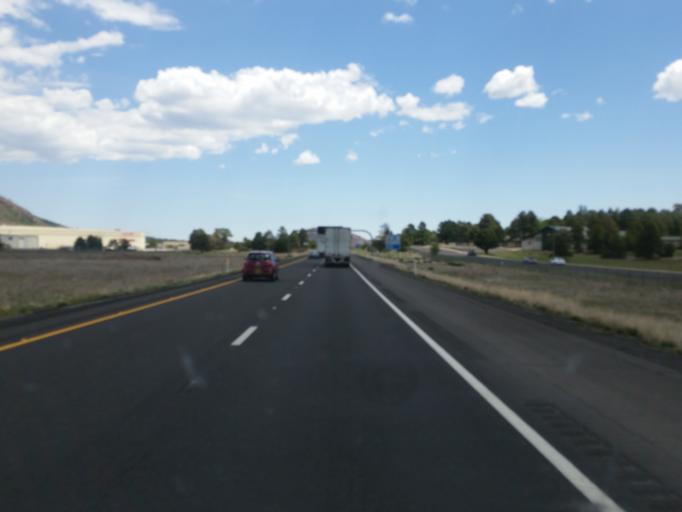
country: US
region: Arizona
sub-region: Coconino County
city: Flagstaff
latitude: 35.2049
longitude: -111.6037
